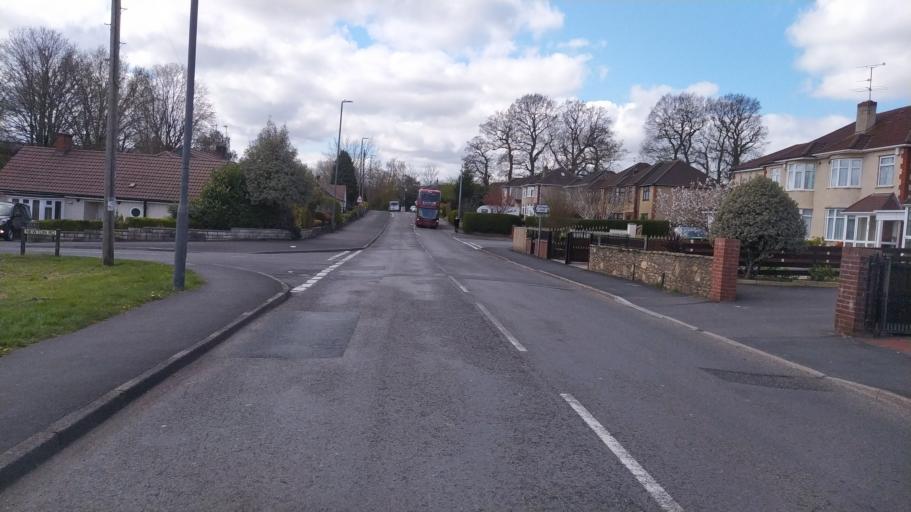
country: GB
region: England
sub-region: South Gloucestershire
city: Kingswood
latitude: 51.4482
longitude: -2.4865
